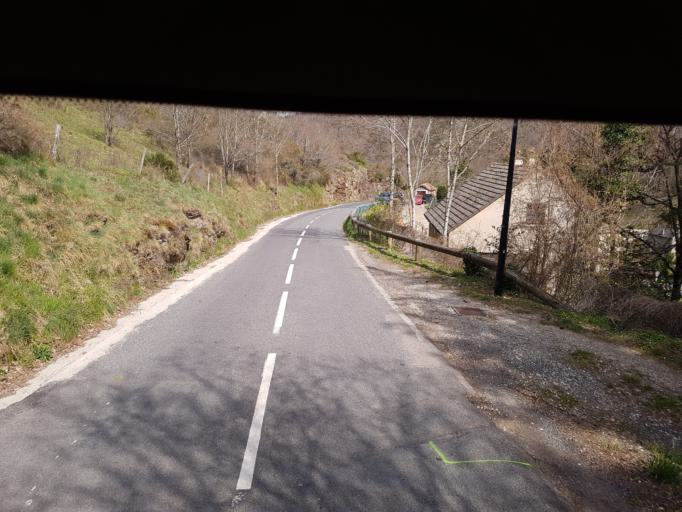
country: FR
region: Languedoc-Roussillon
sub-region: Departement de la Lozere
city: Meyrueis
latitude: 44.2156
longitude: 3.5362
